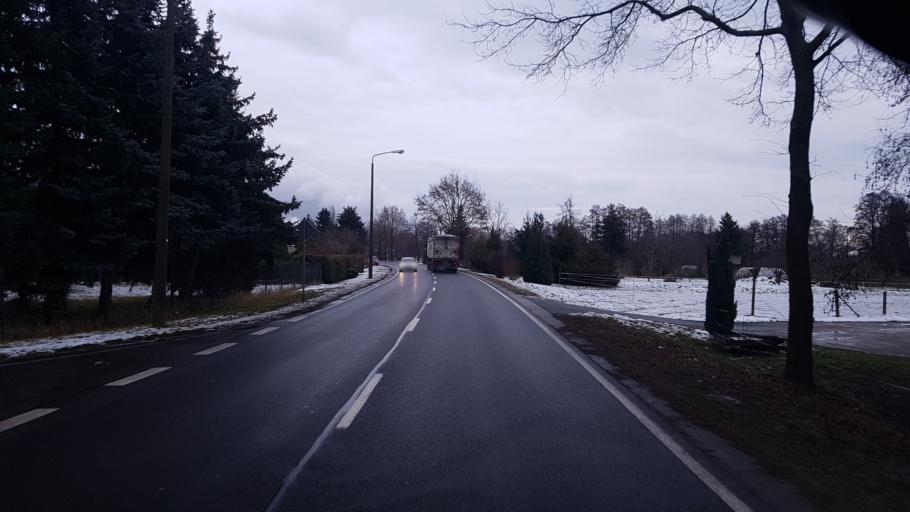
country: DE
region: Brandenburg
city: Peitz
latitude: 51.8504
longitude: 14.4139
